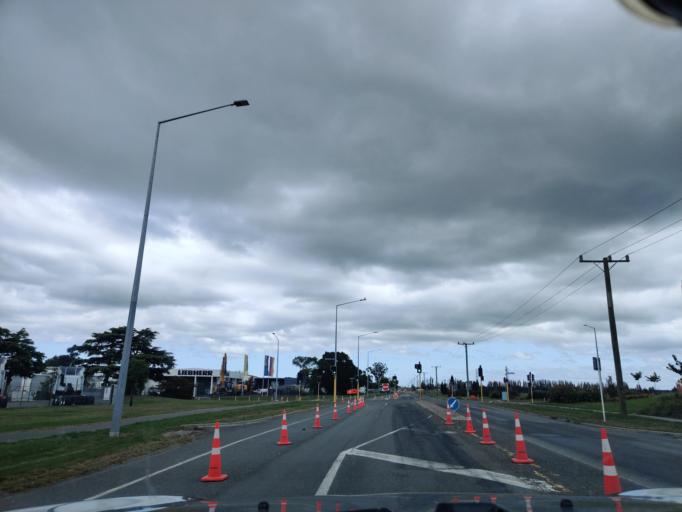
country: NZ
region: Canterbury
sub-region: Selwyn District
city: Prebbleton
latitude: -43.5550
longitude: 172.5128
